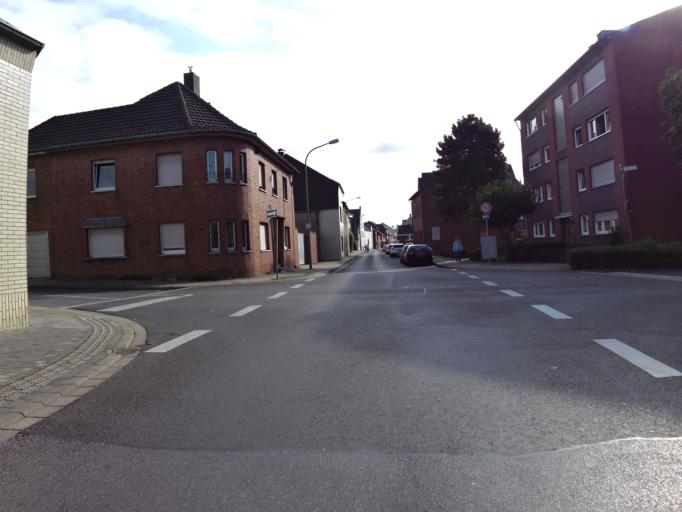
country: DE
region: North Rhine-Westphalia
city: Baesweiler
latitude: 50.9112
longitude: 6.1808
